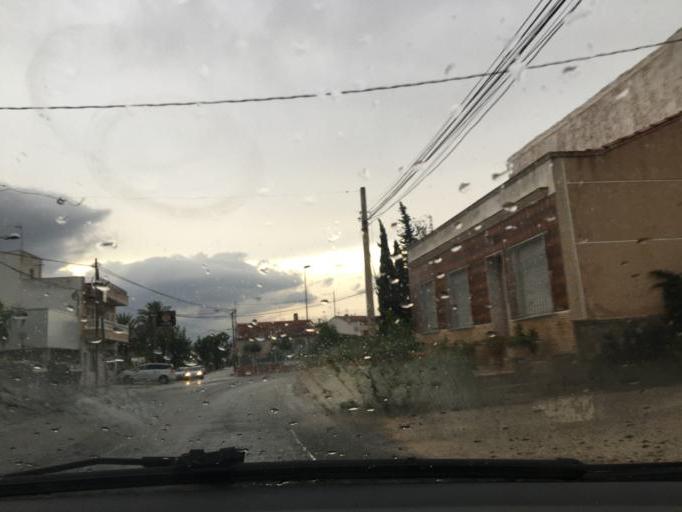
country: ES
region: Murcia
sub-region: Murcia
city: Santomera
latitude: 38.0263
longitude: -1.0467
